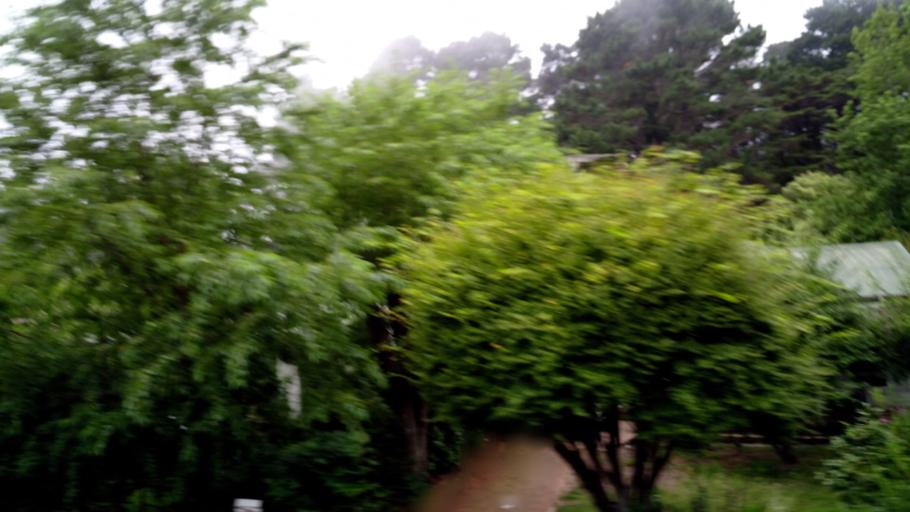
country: AU
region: New South Wales
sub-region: Blue Mountains Municipality
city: Leura
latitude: -33.7231
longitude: 150.3286
